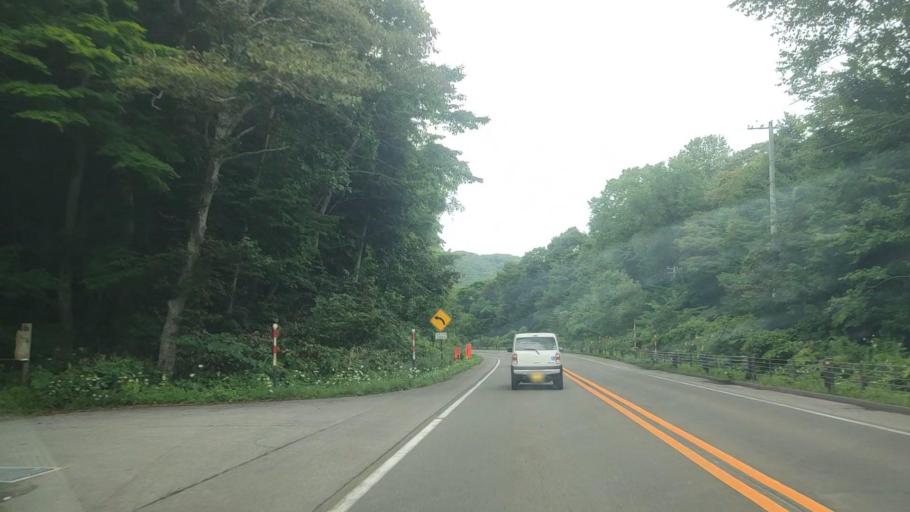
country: JP
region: Hokkaido
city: Nanae
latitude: 41.9712
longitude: 140.6505
